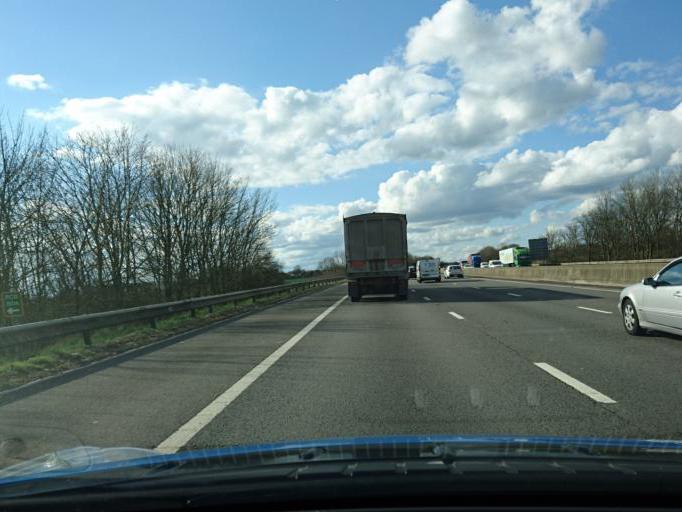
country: GB
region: England
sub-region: Wiltshire
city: Aldbourne
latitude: 51.4875
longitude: -1.5730
